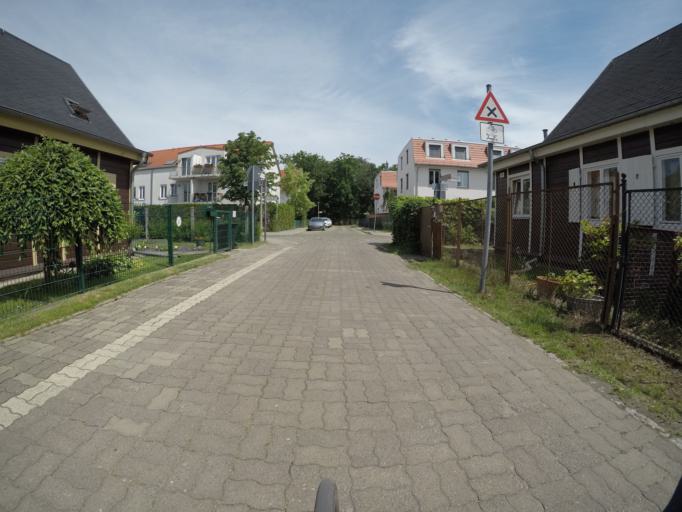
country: DE
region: Berlin
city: Adlershof
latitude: 52.4406
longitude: 13.5436
